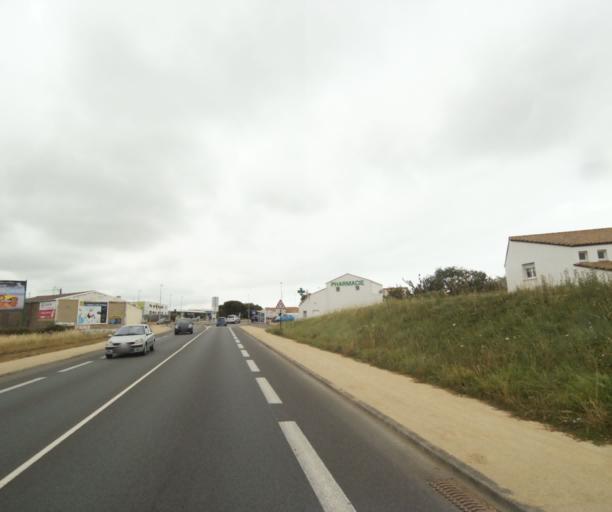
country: FR
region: Pays de la Loire
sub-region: Departement de la Vendee
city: Chateau-d'Olonne
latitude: 46.5002
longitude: -1.7578
